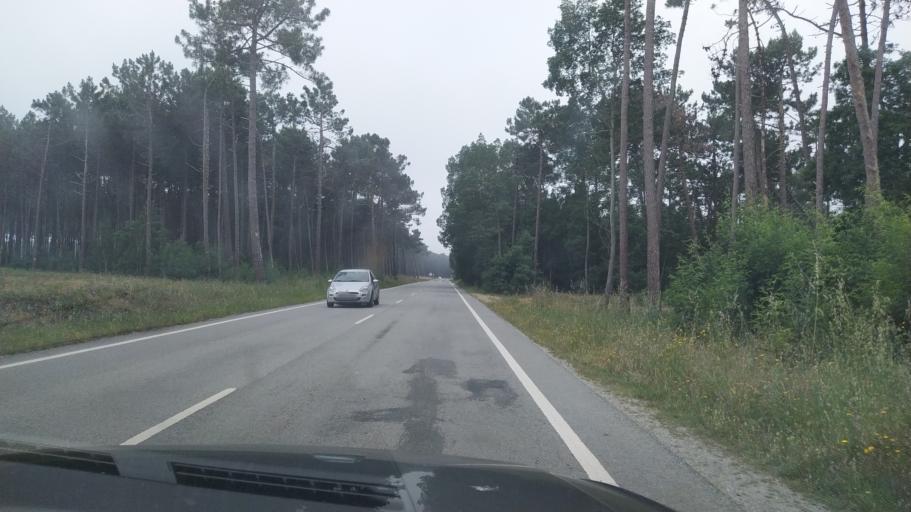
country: PT
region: Aveiro
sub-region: Ilhavo
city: Gafanha da Encarnacao
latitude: 40.6007
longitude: -8.7233
